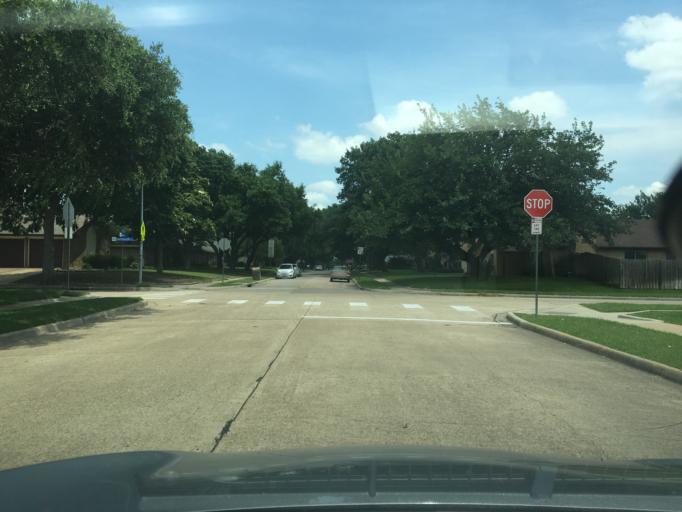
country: US
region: Texas
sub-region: Dallas County
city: Richardson
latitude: 32.9549
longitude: -96.6890
